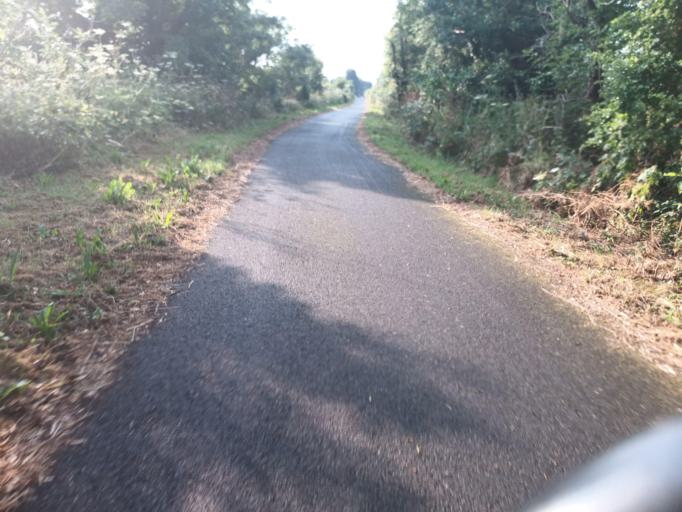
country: GB
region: Northern Ireland
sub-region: Castlereagh District
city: Dundonald
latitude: 54.5702
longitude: -5.7713
